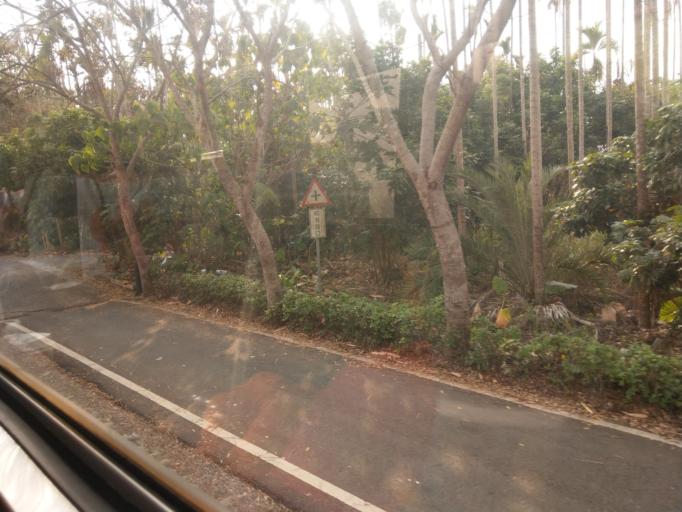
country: TW
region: Taiwan
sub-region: Chiayi
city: Jiayi Shi
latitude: 23.5172
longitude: 120.5474
